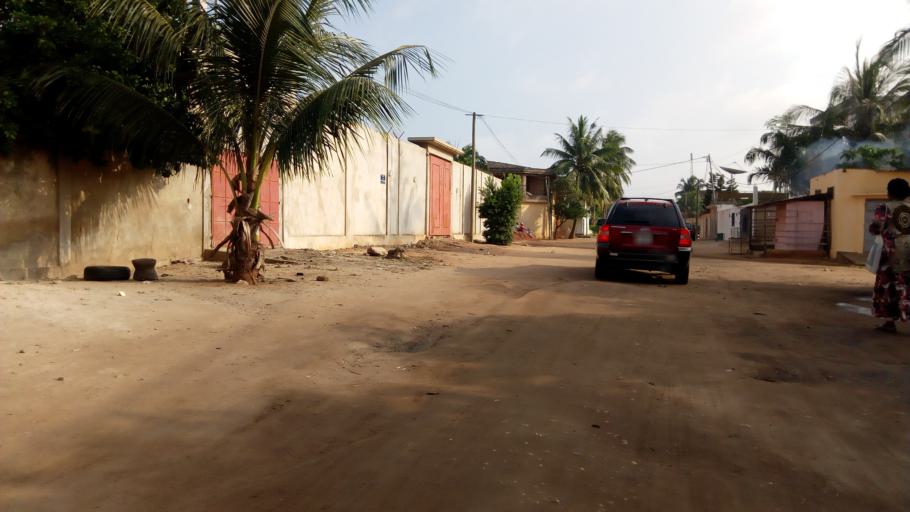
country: TG
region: Maritime
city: Lome
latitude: 6.1722
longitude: 1.1799
